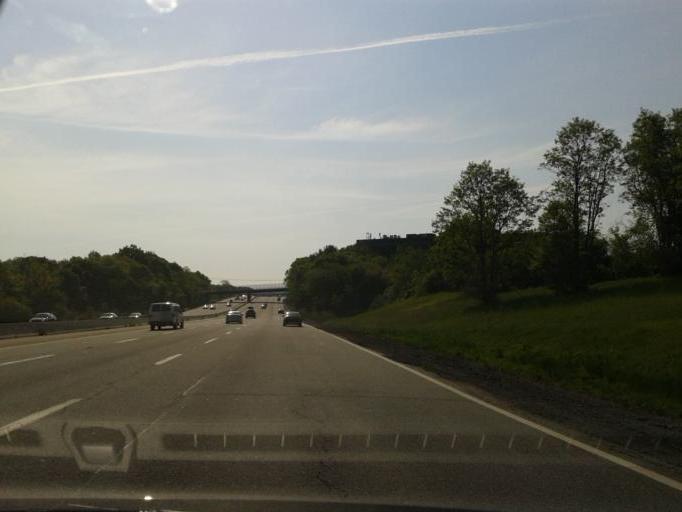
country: US
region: Massachusetts
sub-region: Middlesex County
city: Cochituate
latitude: 42.3143
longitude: -71.3951
